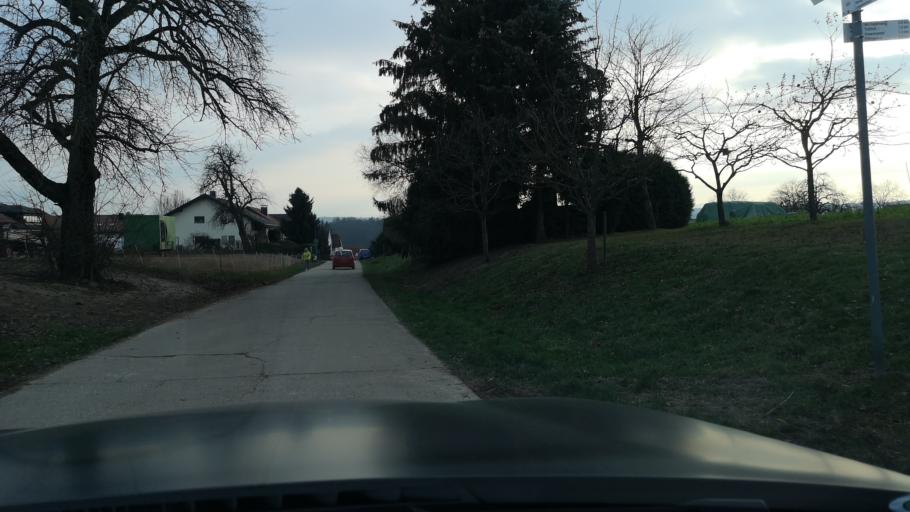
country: DE
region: Baden-Wuerttemberg
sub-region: Karlsruhe Region
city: Ettlingen
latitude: 48.9358
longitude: 8.4606
